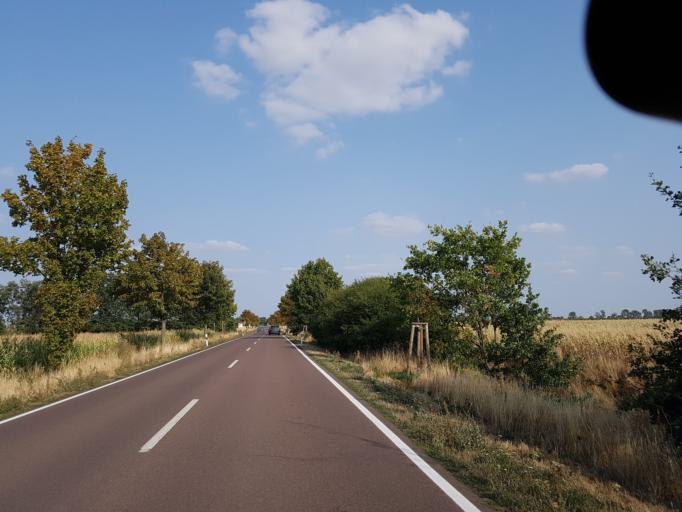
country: DE
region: Saxony-Anhalt
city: Kemberg
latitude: 51.8061
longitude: 12.6615
